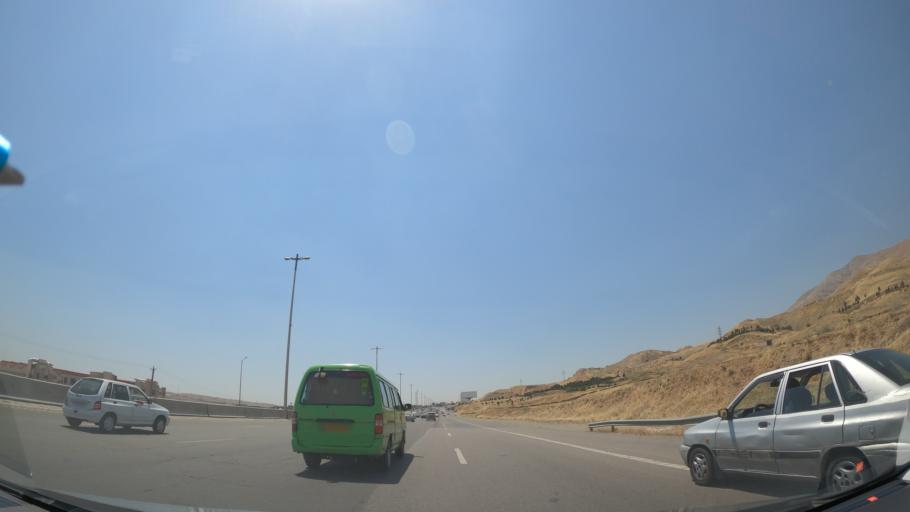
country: IR
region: Tehran
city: Shahr-e Qods
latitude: 35.7427
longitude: 51.1103
